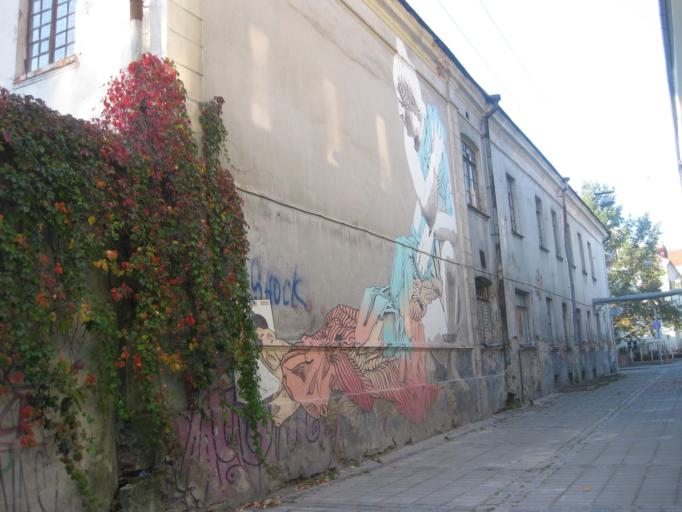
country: LT
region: Kauno apskritis
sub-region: Kaunas
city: Kaunas
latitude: 54.8953
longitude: 23.8878
